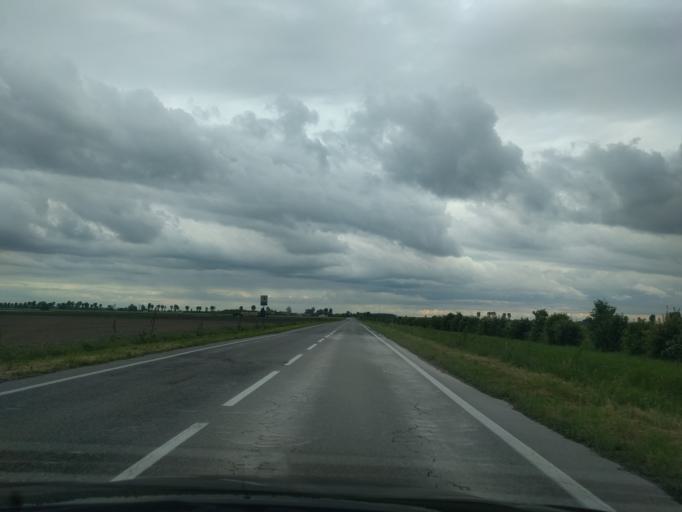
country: IT
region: Veneto
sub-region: Provincia di Rovigo
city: Buso
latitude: 45.0853
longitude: 11.8517
